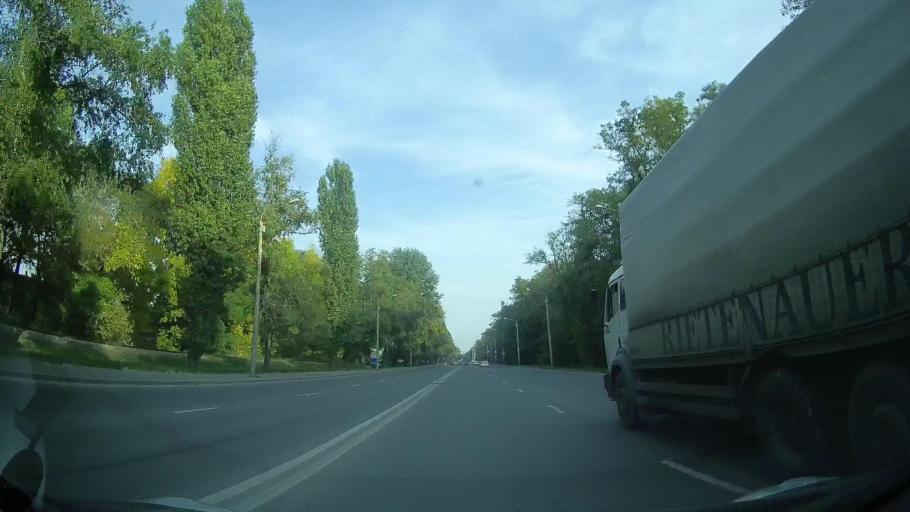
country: RU
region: Rostov
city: Imeni Chkalova
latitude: 47.2768
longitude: 39.8047
